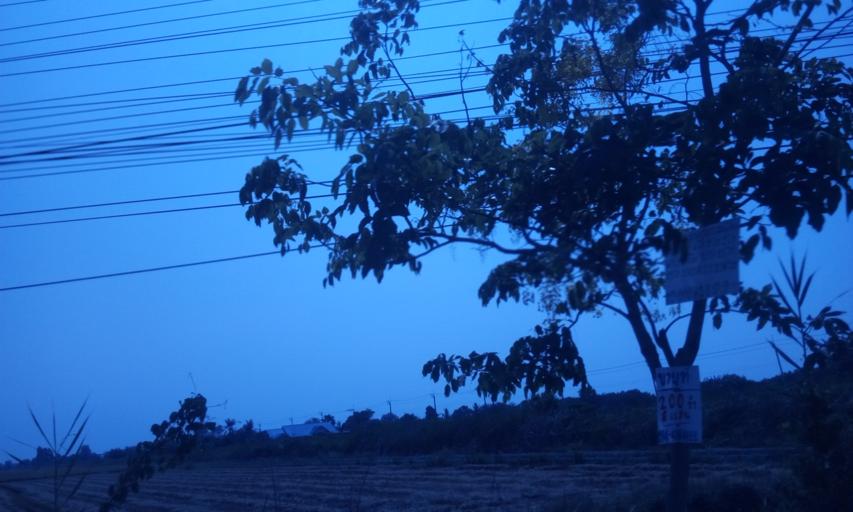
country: TH
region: Nonthaburi
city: Sai Noi
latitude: 13.9542
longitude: 100.3115
